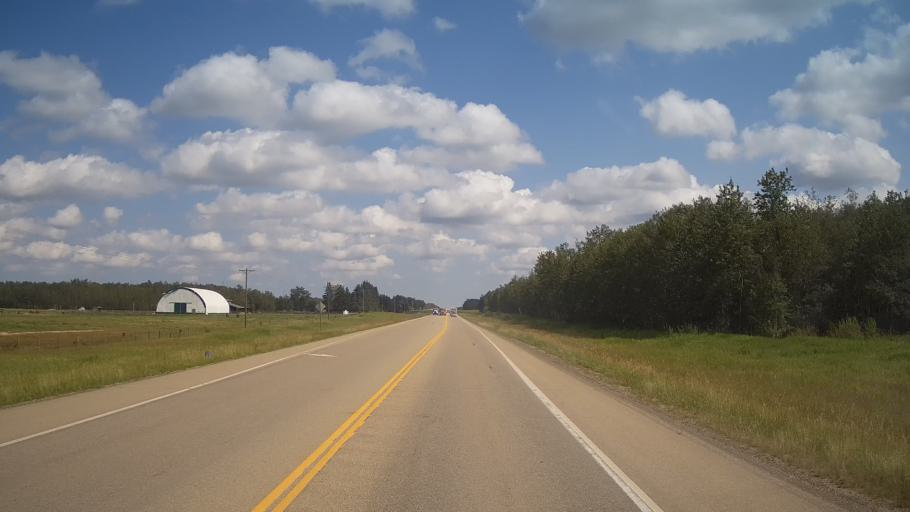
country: CA
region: Alberta
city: Sherwood Park
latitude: 53.3957
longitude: -113.0712
